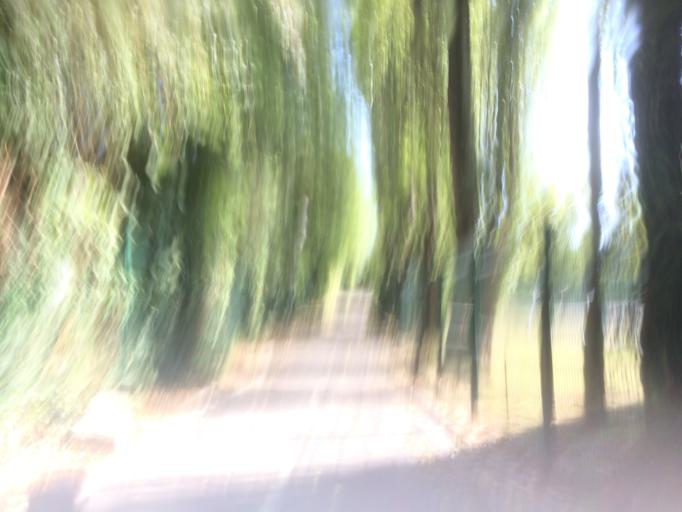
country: FR
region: Ile-de-France
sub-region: Departement de l'Essonne
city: Longjumeau
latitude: 48.6953
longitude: 2.3152
